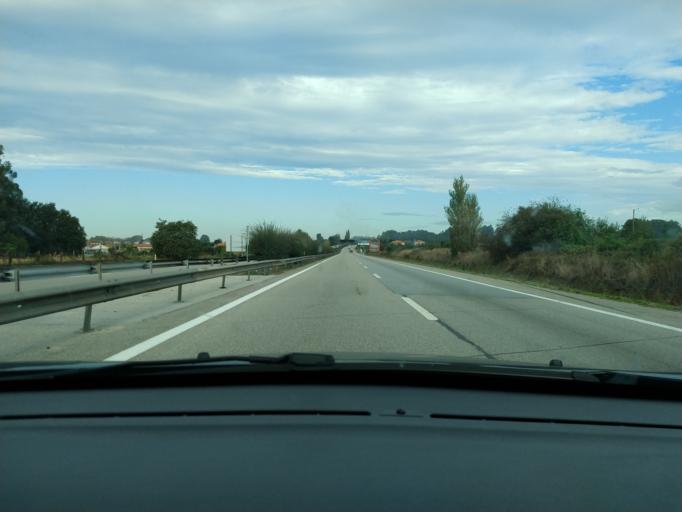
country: PT
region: Aveiro
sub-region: Estarreja
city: Beduido
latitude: 40.7617
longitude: -8.5399
